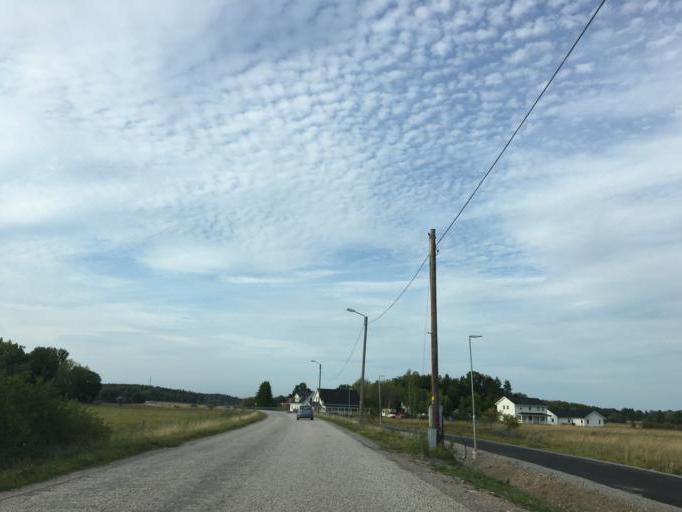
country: SE
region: Soedermanland
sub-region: Eskilstuna Kommun
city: Torshalla
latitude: 59.4366
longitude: 16.4758
